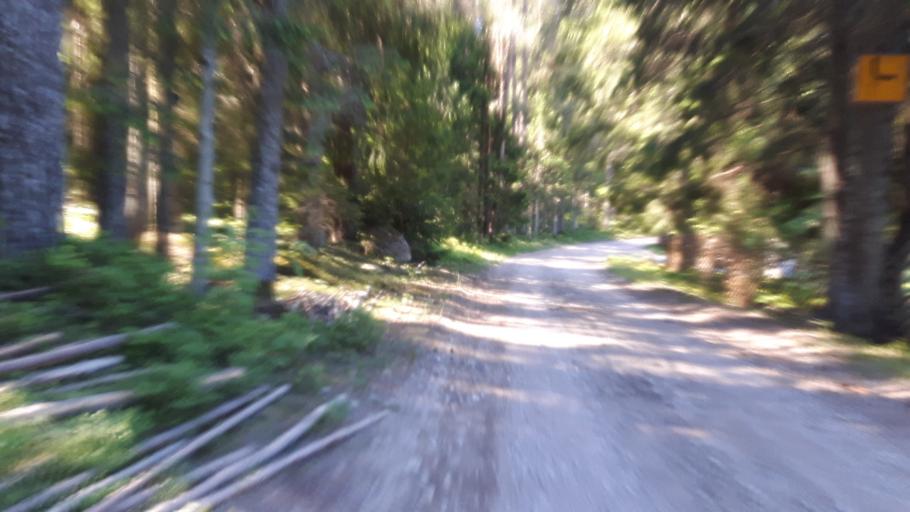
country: EE
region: Harju
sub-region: Loksa linn
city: Loksa
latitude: 59.5606
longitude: 25.8194
